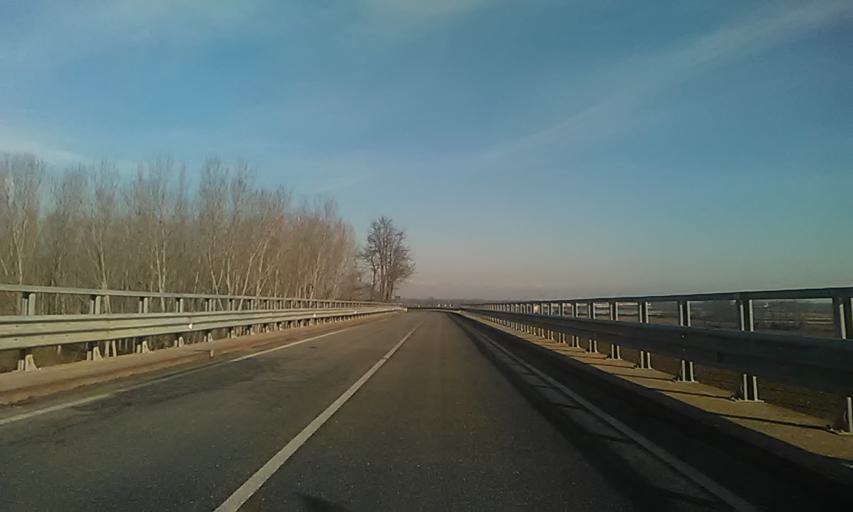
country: IT
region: Piedmont
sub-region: Provincia di Vercelli
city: Formigliana
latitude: 45.4331
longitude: 8.2971
